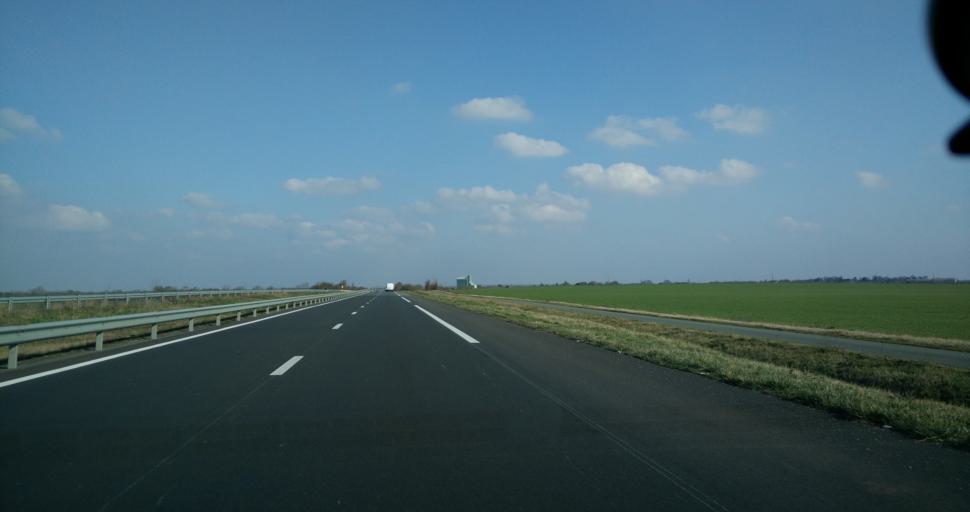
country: FR
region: Poitou-Charentes
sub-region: Departement de la Charente-Maritime
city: Sainte-Soulle
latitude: 46.2082
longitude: -1.0096
